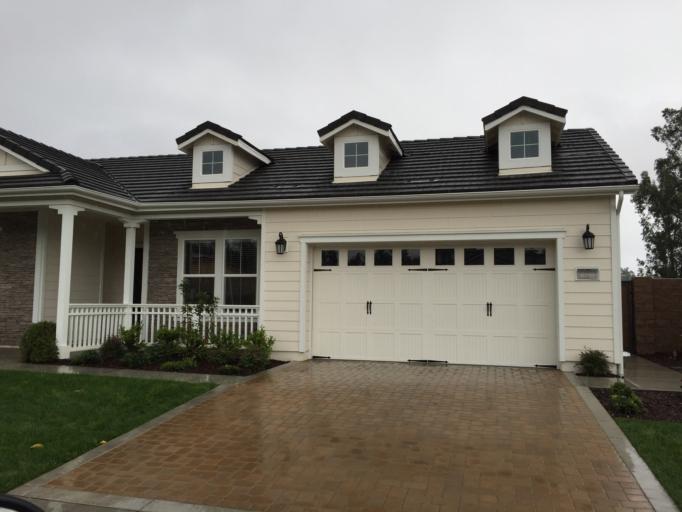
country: US
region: California
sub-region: San Luis Obispo County
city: Callender
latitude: 35.0326
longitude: -120.5433
